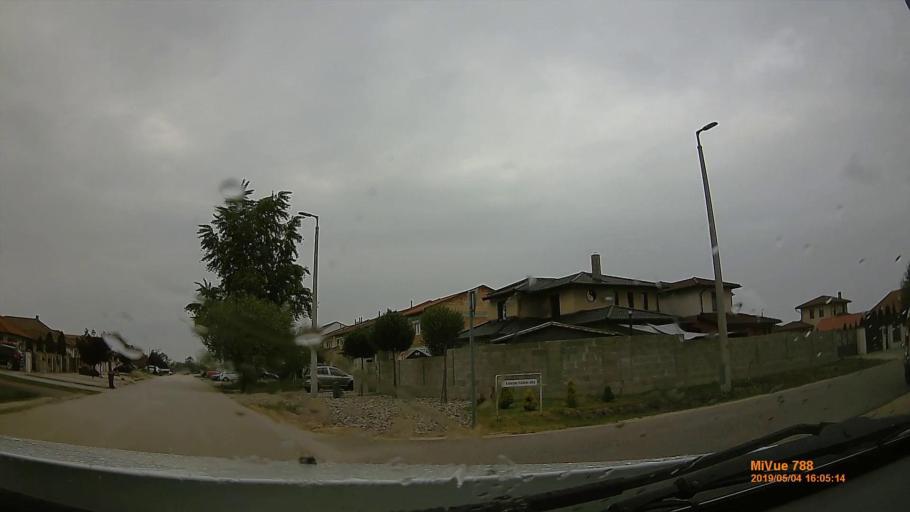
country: HU
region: Gyor-Moson-Sopron
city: Mosonmagyarovar
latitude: 47.8890
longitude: 17.2897
